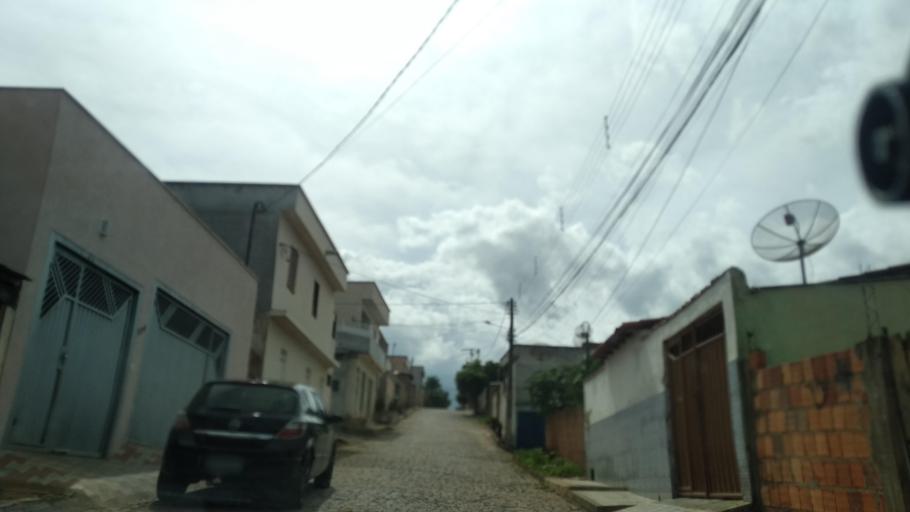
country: BR
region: Bahia
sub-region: Caetite
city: Caetite
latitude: -14.0636
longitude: -42.4807
